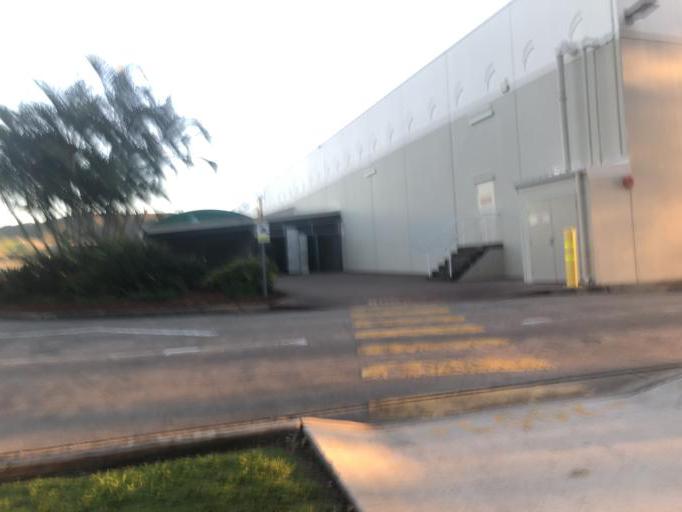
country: AU
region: New South Wales
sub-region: Coffs Harbour
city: Coffs Harbour
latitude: -30.2847
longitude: 153.1314
